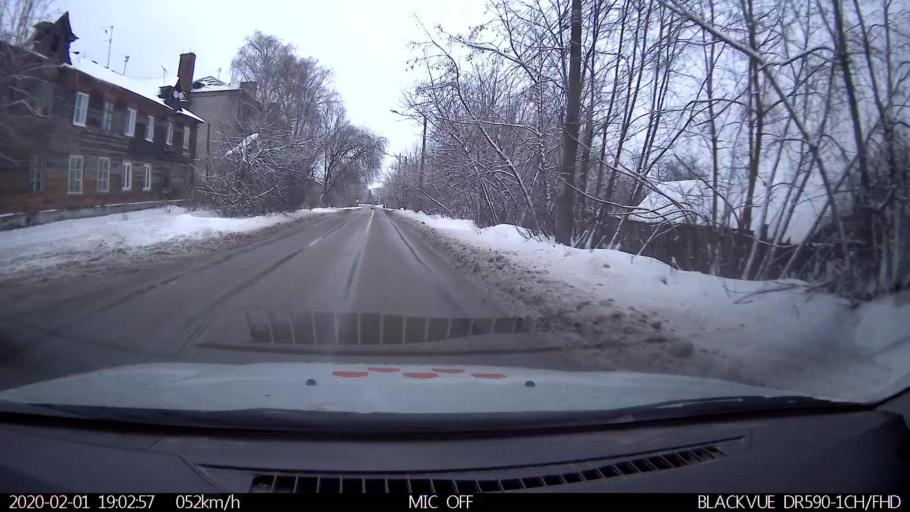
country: RU
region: Nizjnij Novgorod
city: Nizhniy Novgorod
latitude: 56.2985
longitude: 44.0066
